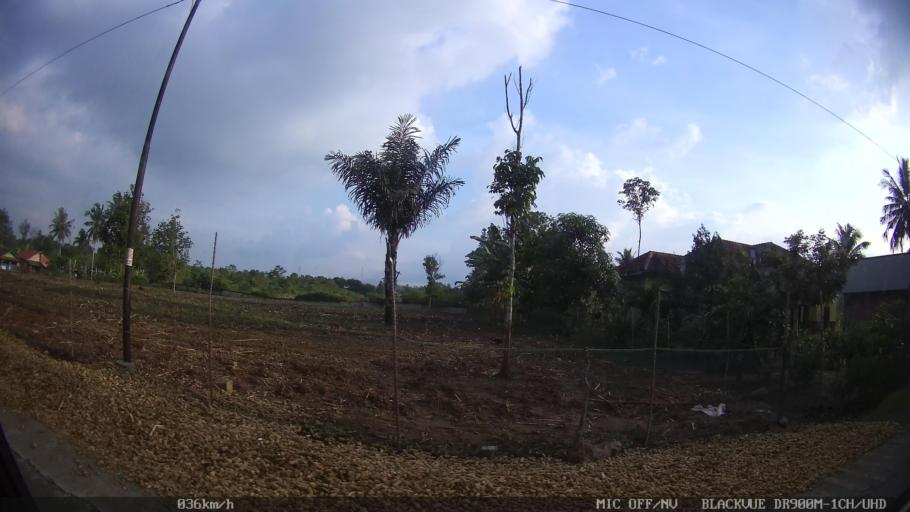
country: ID
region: Lampung
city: Panjang
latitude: -5.3928
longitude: 105.3483
